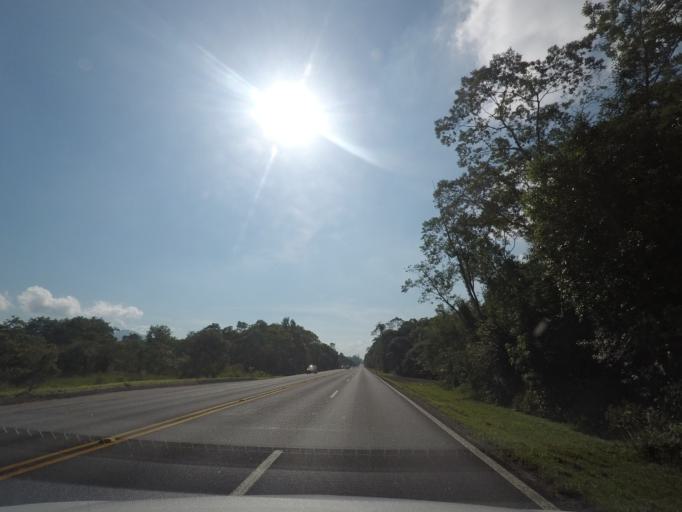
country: BR
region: Parana
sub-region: Pontal Do Parana
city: Pontal do Parana
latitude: -25.6195
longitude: -48.6005
